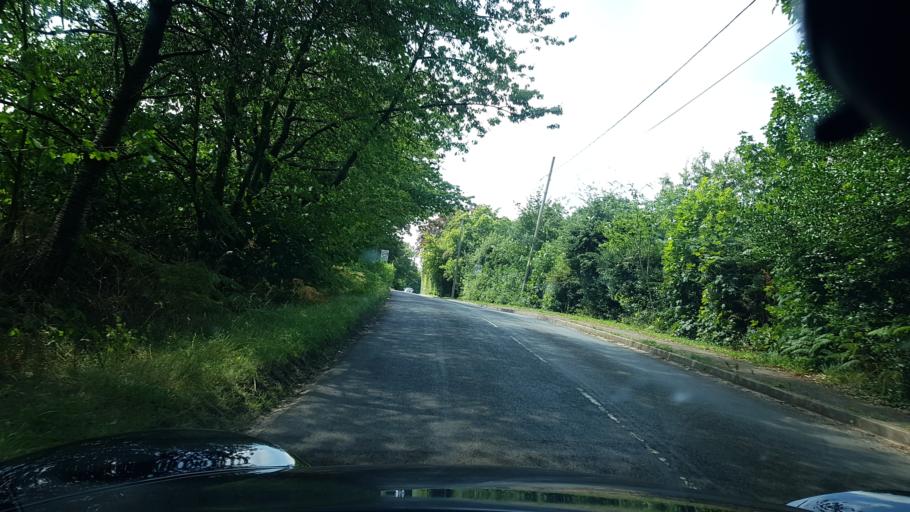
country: GB
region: England
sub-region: Surrey
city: Elstead
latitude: 51.1500
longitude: -0.7074
